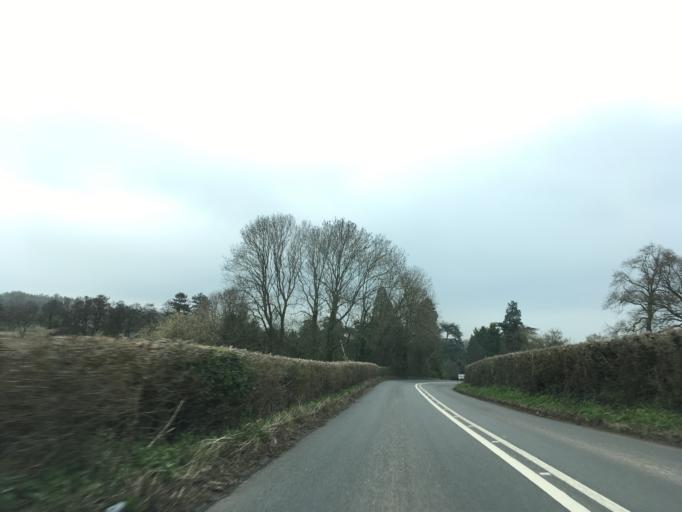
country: GB
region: Wales
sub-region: Monmouthshire
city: Llangybi
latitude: 51.6521
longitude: -2.9168
